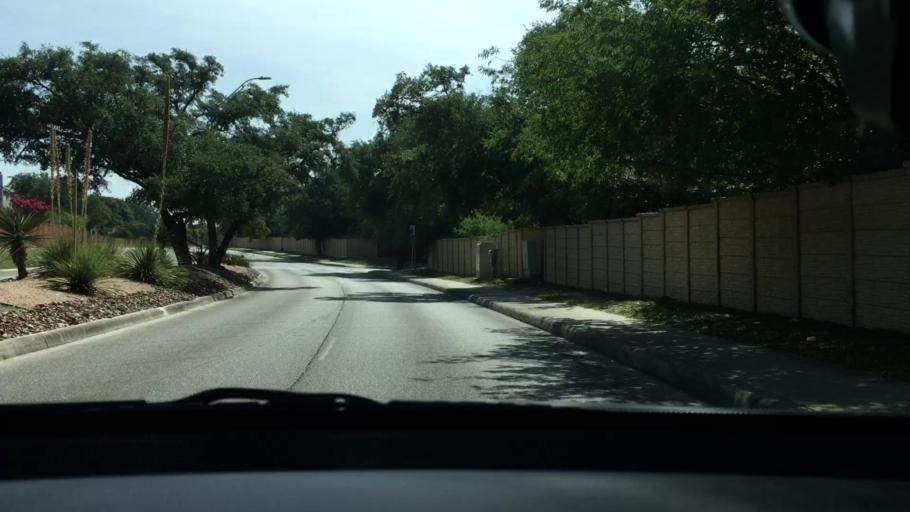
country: US
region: Texas
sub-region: Bexar County
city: Live Oak
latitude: 29.5881
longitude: -98.4006
